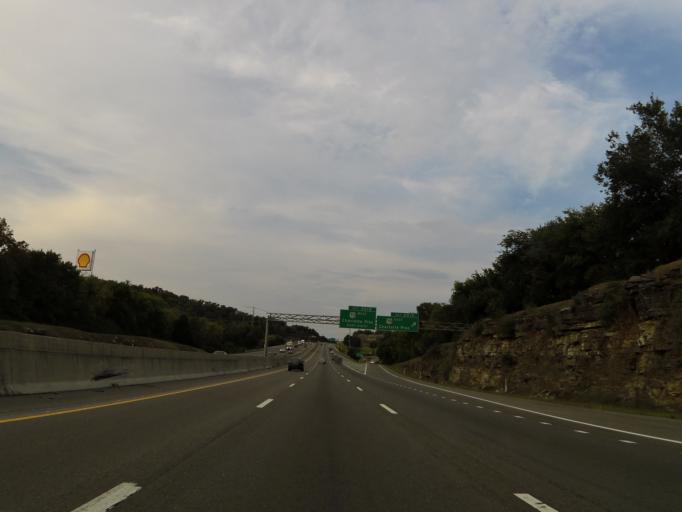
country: US
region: Tennessee
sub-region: Davidson County
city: Belle Meade
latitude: 36.1280
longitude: -86.9009
